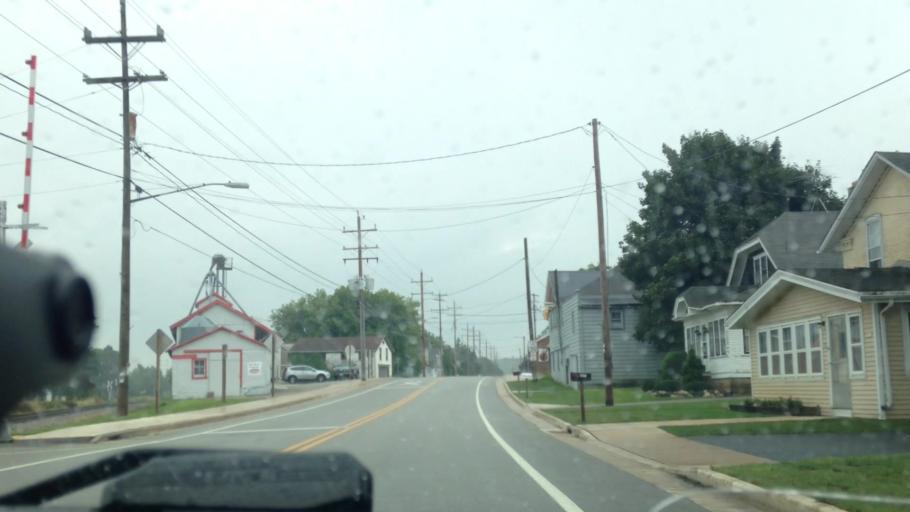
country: US
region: Wisconsin
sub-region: Washington County
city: Richfield
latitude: 43.2591
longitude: -88.1960
